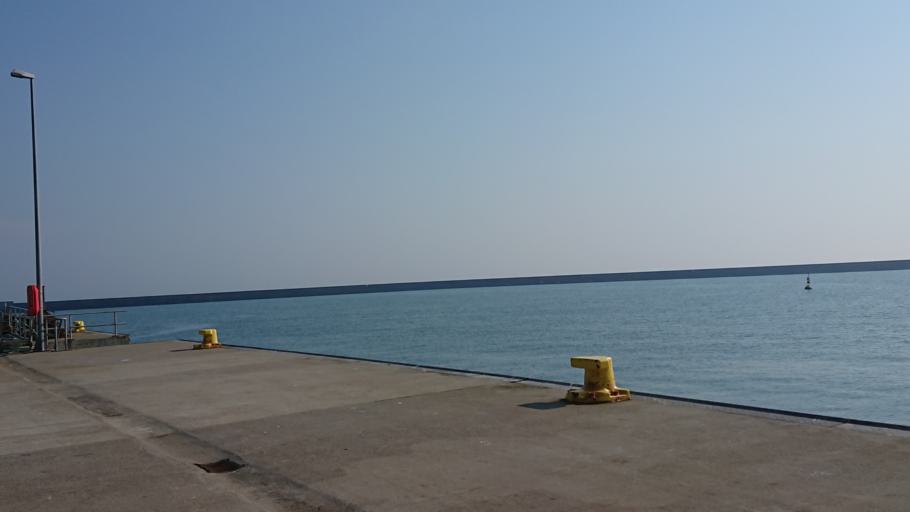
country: DE
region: Schleswig-Holstein
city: Helgoland
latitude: 54.1738
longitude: 7.8942
